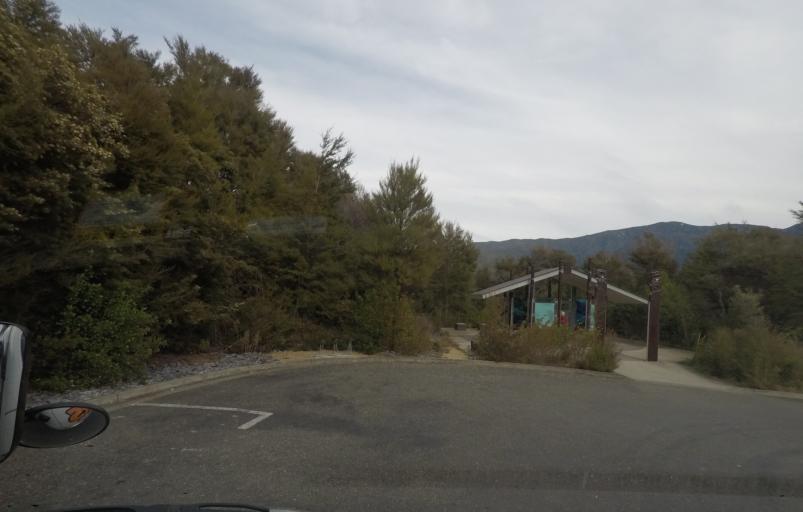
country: NZ
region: Tasman
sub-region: Tasman District
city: Takaka
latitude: -40.8482
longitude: 172.7708
